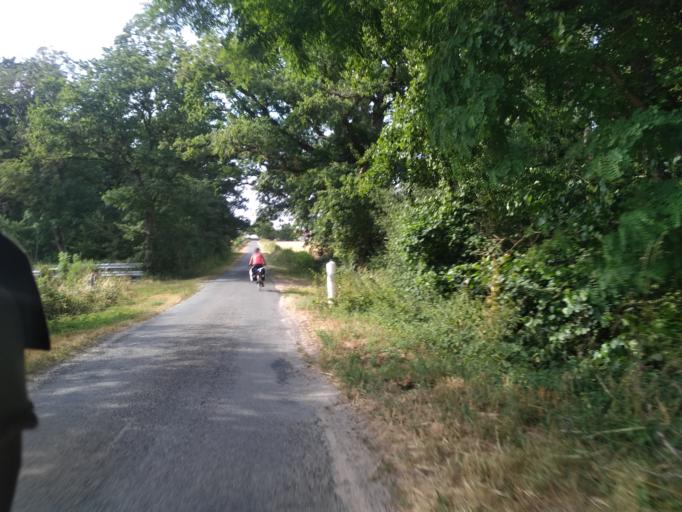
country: FR
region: Bourgogne
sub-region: Departement de Saone-et-Loire
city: Bourbon-Lancy
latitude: 46.6623
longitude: 3.7626
